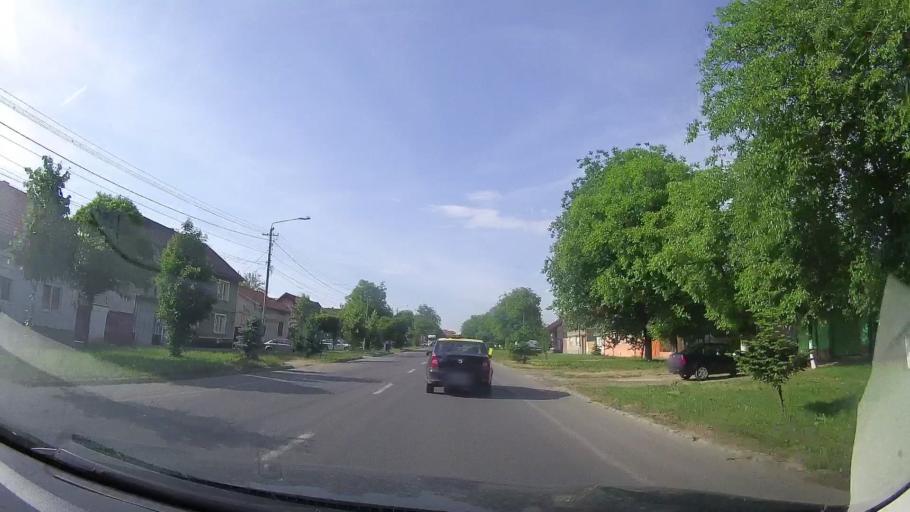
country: RO
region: Caras-Severin
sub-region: Municipiul Caransebes
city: Caransebes
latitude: 45.3995
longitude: 22.2249
